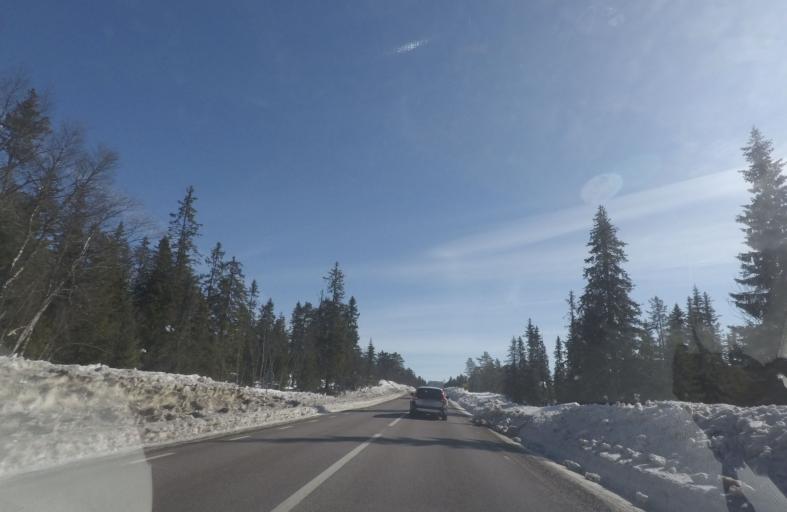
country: NO
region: Hedmark
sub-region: Trysil
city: Innbygda
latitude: 61.1774
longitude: 13.0547
